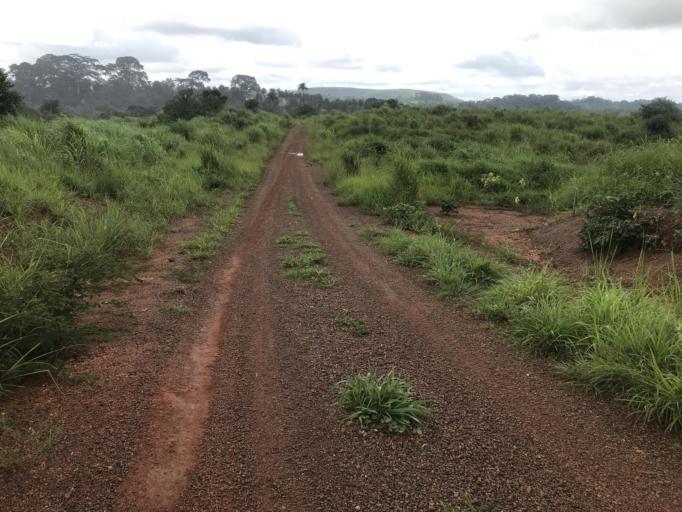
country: GN
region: Nzerekore
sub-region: Prefecture de Guekedou
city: Gueckedou
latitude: 8.4753
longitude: -10.2892
